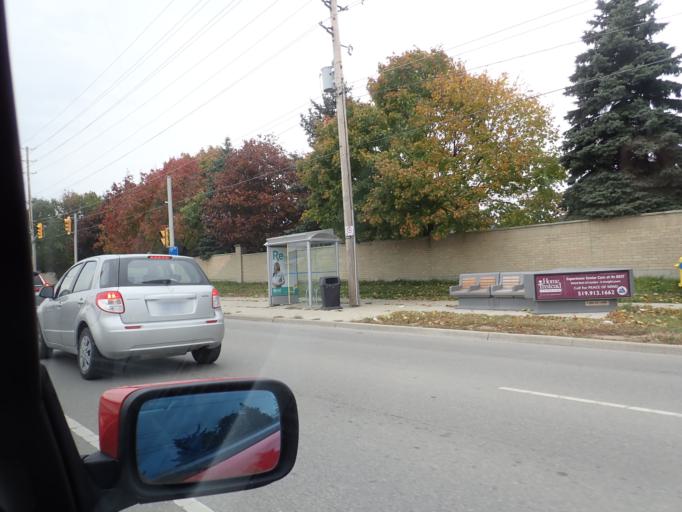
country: CA
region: Ontario
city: London
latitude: 42.9393
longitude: -81.2780
